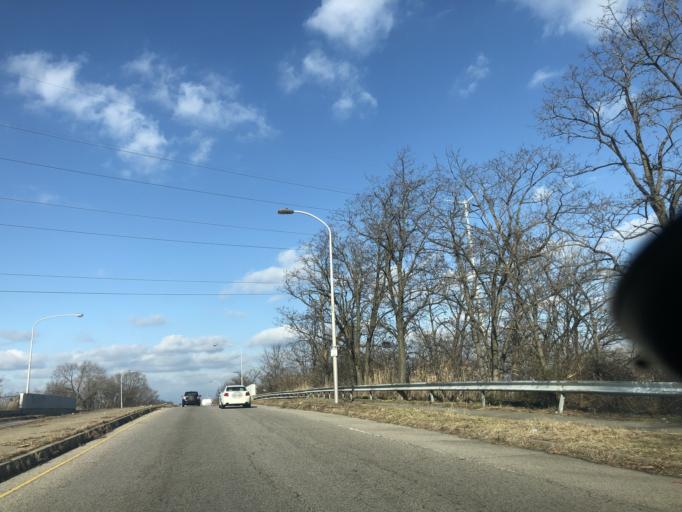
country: US
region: Pennsylvania
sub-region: Delaware County
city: Colwyn
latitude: 39.9084
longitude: -75.2287
